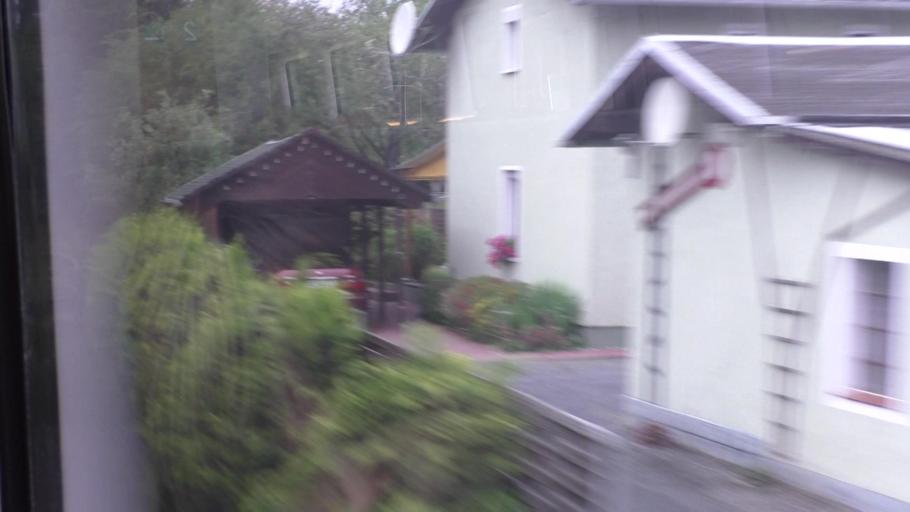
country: DE
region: Saxony
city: Eibau
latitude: 50.9739
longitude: 14.6880
